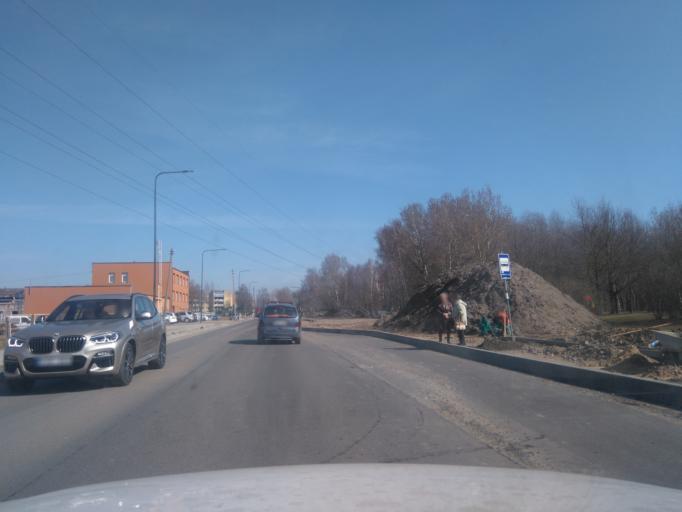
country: LT
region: Kauno apskritis
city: Dainava (Kaunas)
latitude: 54.8840
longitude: 23.9504
